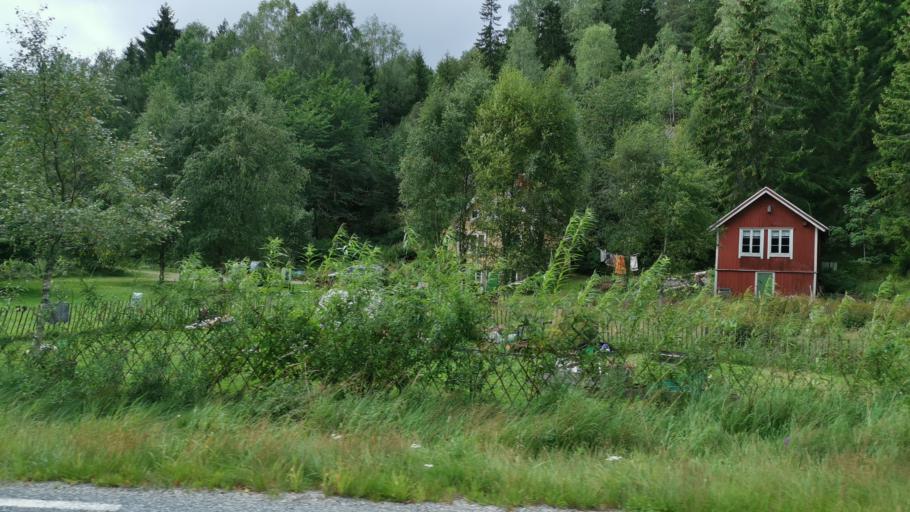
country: SE
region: Vaestra Goetaland
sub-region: Lysekils Kommun
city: Brastad
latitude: 58.4700
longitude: 11.4251
